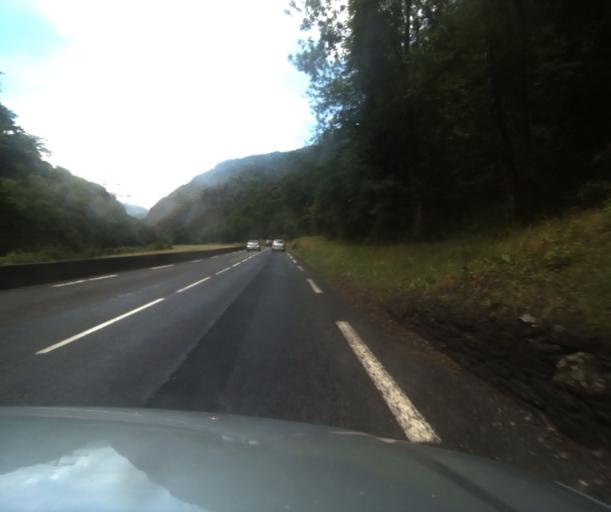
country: FR
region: Midi-Pyrenees
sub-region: Departement des Hautes-Pyrenees
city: Pierrefitte-Nestalas
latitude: 42.9431
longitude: -0.0531
